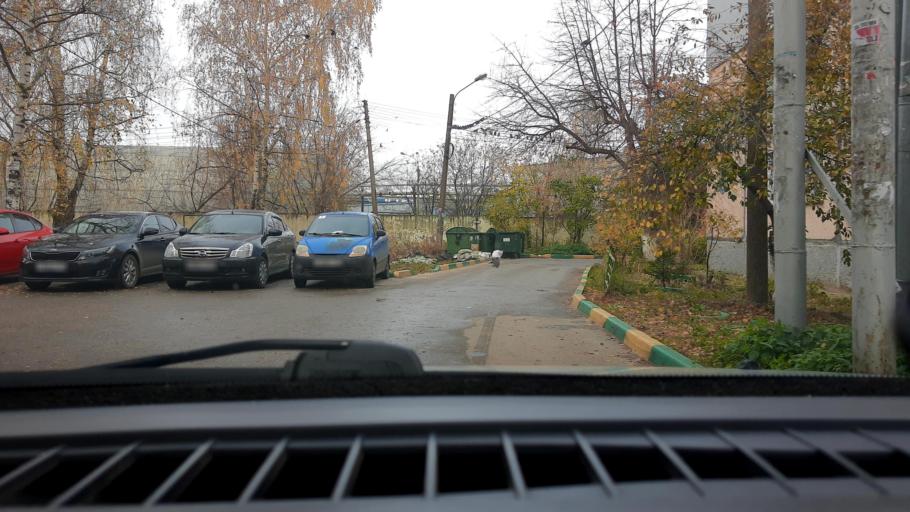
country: RU
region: Nizjnij Novgorod
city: Nizhniy Novgorod
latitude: 56.2581
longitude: 43.9208
